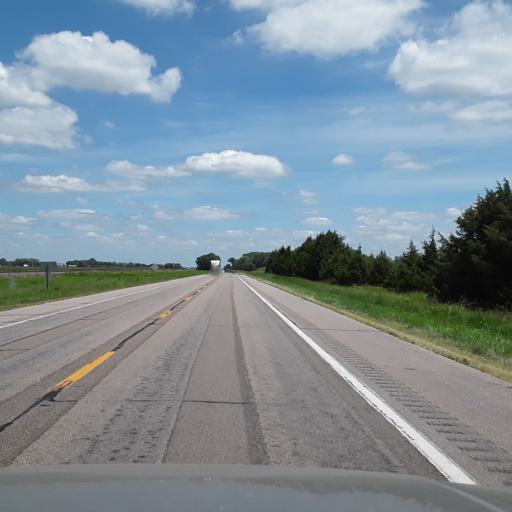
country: US
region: Nebraska
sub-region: Nance County
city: Genoa
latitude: 41.3439
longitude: -97.5974
